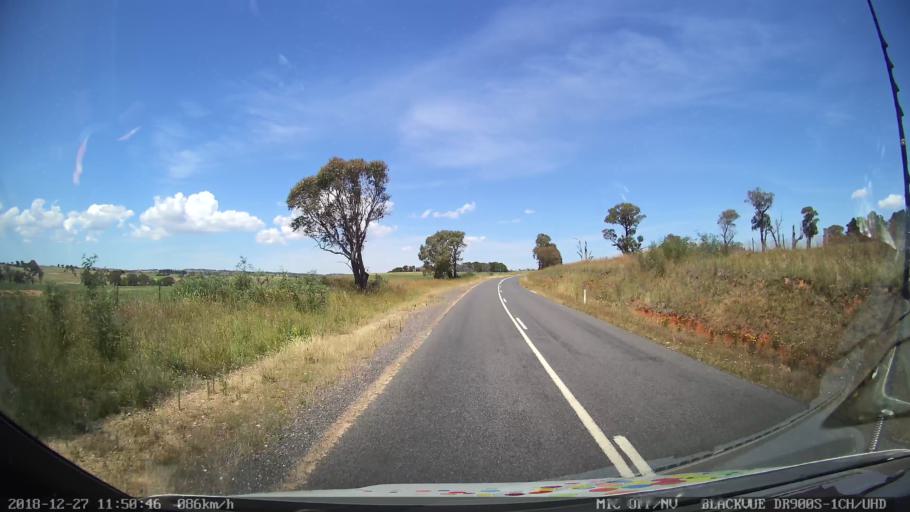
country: AU
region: New South Wales
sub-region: Bathurst Regional
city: Perthville
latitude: -33.6353
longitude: 149.4279
